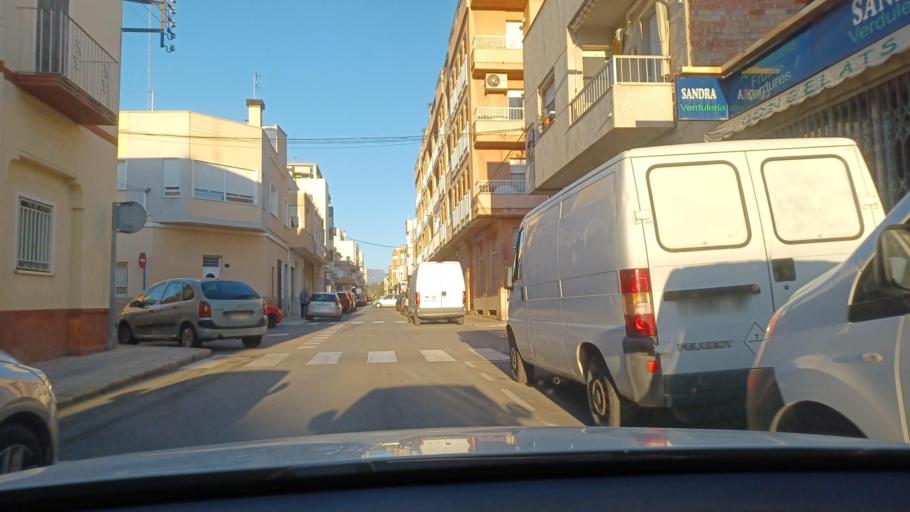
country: ES
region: Catalonia
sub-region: Provincia de Tarragona
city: Amposta
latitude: 40.7119
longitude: 0.5760
